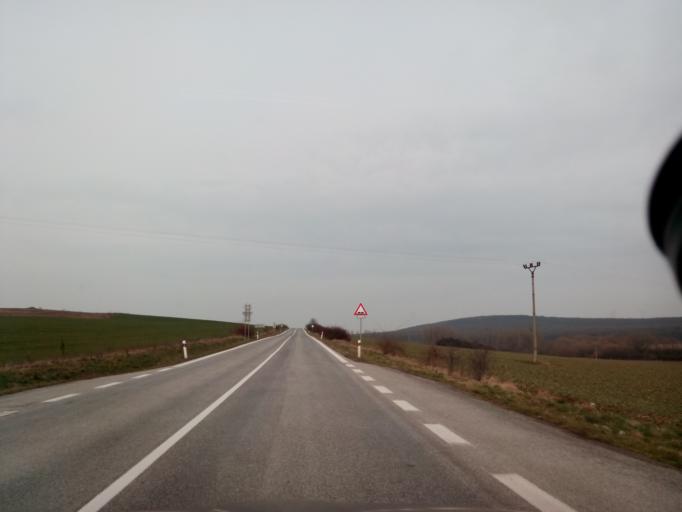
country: HU
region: Borsod-Abauj-Zemplen
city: Satoraljaujhely
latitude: 48.4826
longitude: 21.6450
